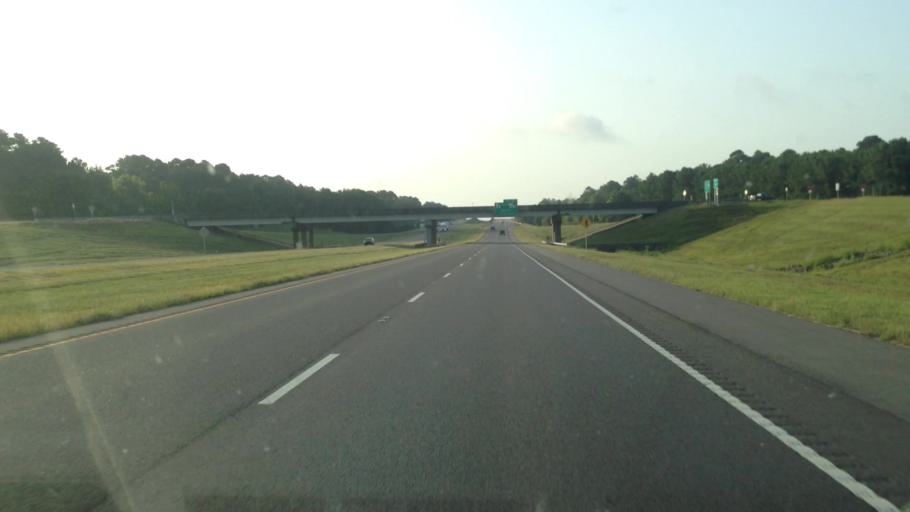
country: US
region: Louisiana
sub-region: Rapides Parish
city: Boyce
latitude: 31.4106
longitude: -92.7187
